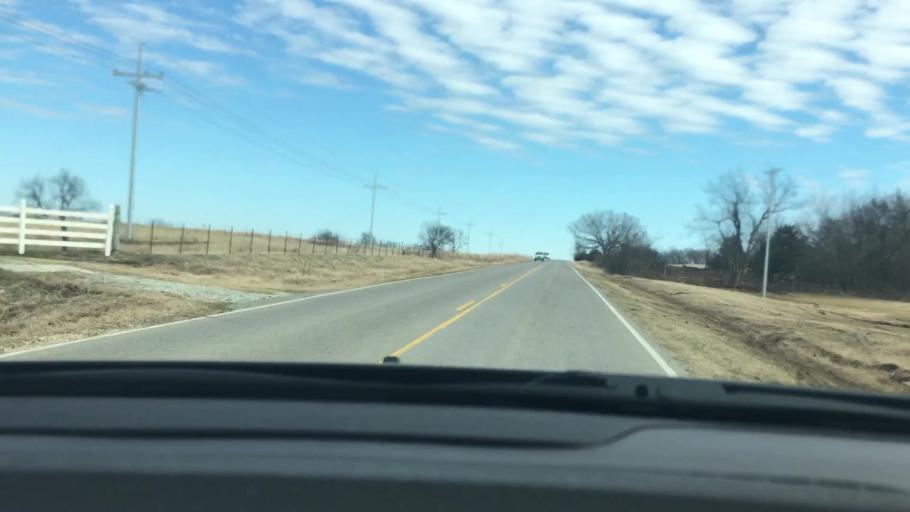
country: US
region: Oklahoma
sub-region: Garvin County
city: Stratford
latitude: 34.7966
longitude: -96.9292
